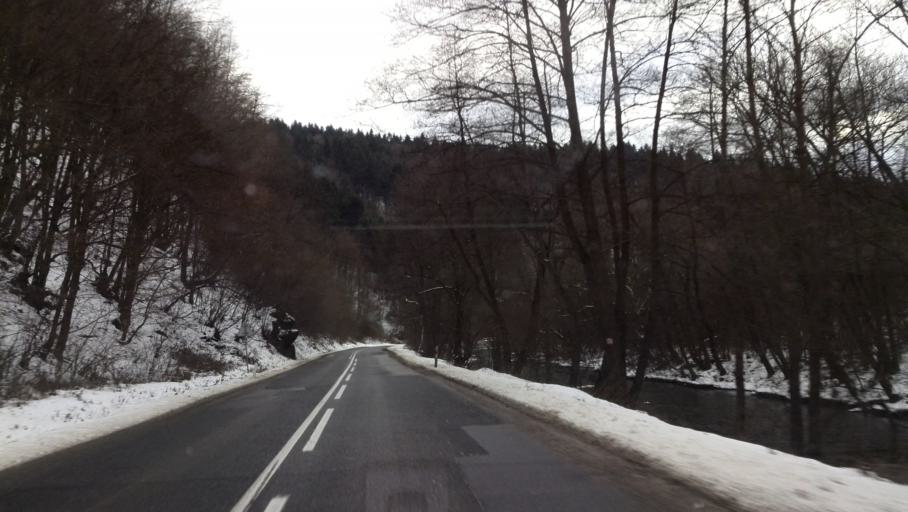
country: SK
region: Kosicky
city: Gelnica
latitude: 48.8690
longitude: 20.9765
